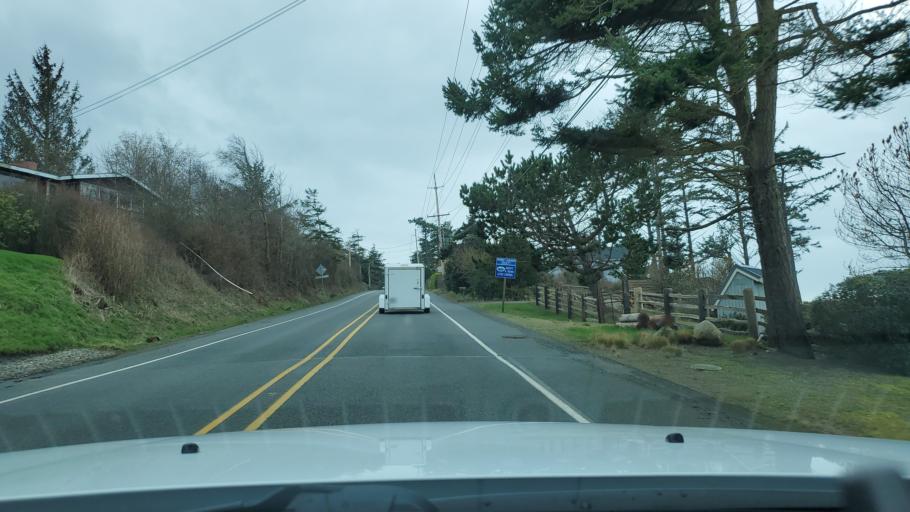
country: US
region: Washington
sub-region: Island County
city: Coupeville
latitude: 48.2641
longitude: -122.7473
